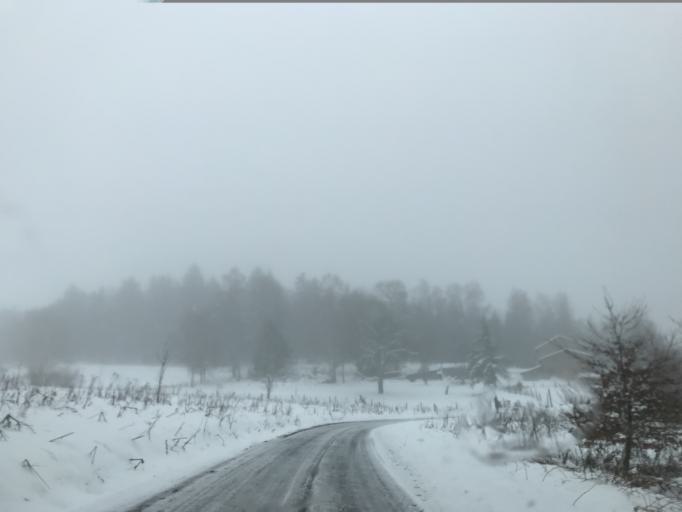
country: FR
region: Auvergne
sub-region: Departement du Puy-de-Dome
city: Job
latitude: 45.7181
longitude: 3.6985
